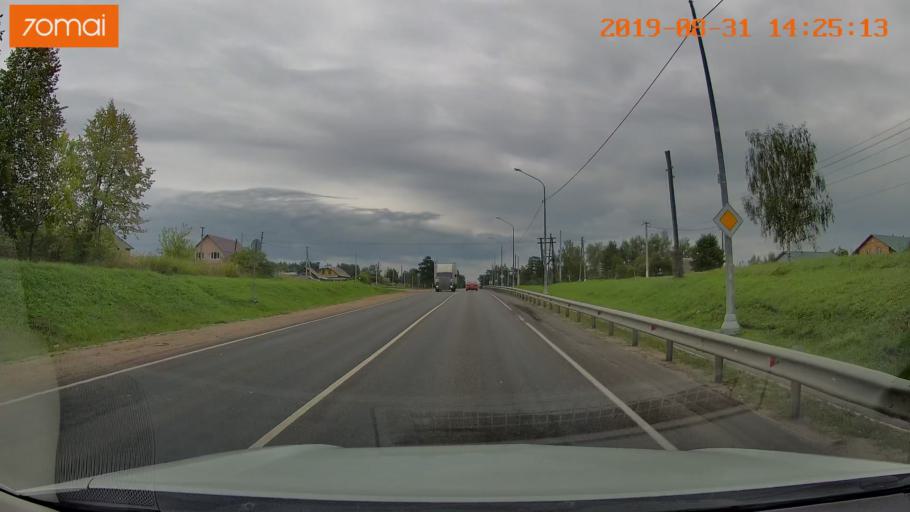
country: RU
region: Smolensk
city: Yekimovichi
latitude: 54.1072
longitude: 33.2694
